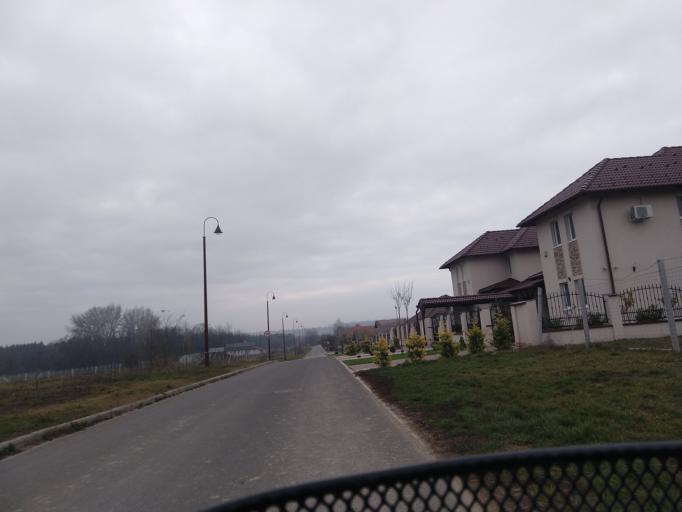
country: HU
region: Pest
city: Orbottyan
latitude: 47.6640
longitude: 19.2577
